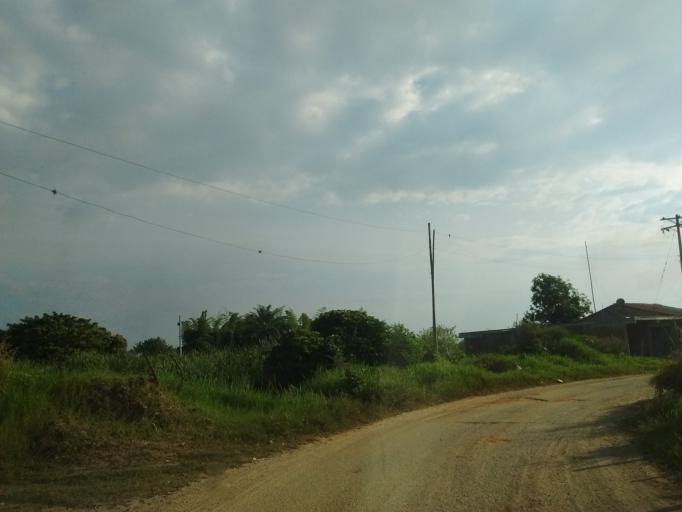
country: CO
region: Cauca
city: Puerto Tejada
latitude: 3.2008
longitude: -76.4404
